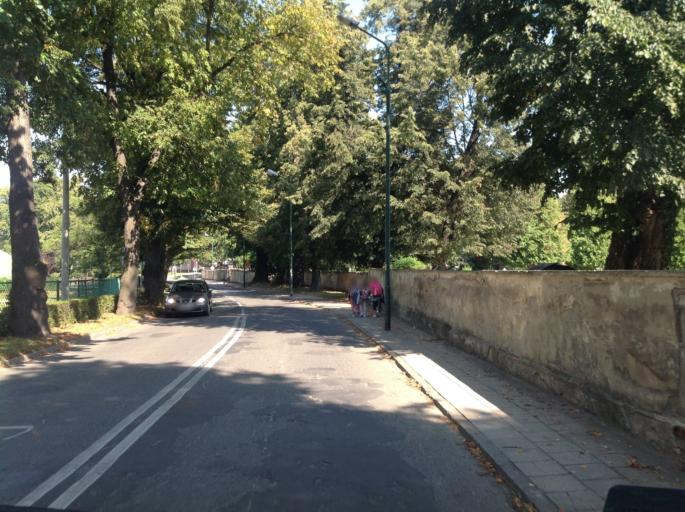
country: PL
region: Lower Silesian Voivodeship
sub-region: Powiat zabkowicki
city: Ziebice
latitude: 50.5993
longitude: 17.0448
